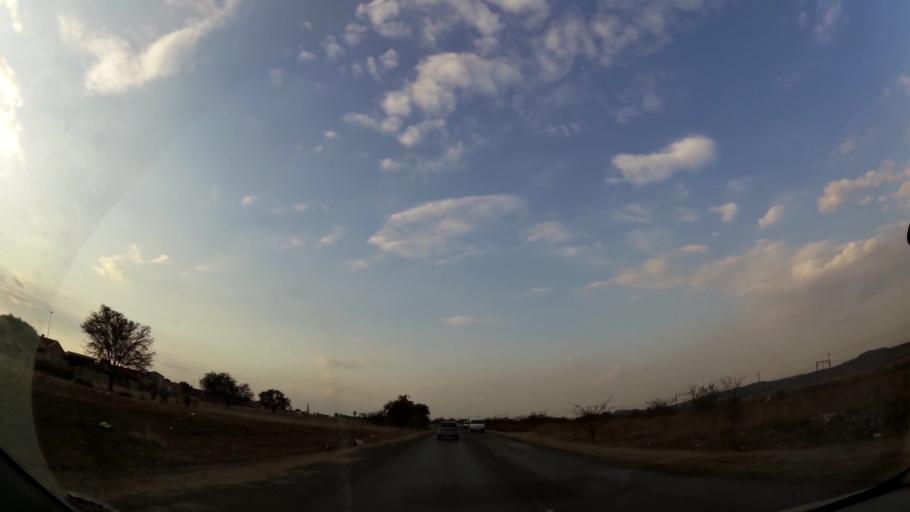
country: ZA
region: Gauteng
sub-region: City of Johannesburg Metropolitan Municipality
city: Orange Farm
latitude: -26.5880
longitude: 27.8527
